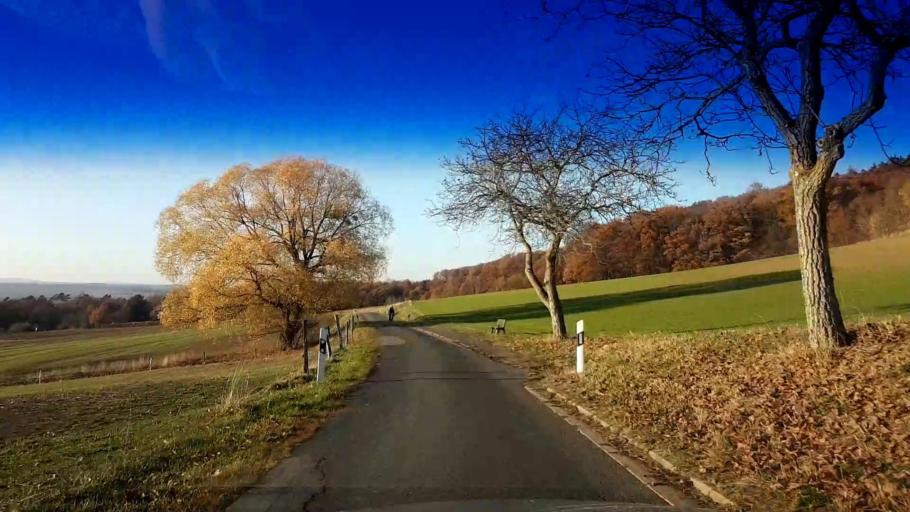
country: DE
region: Bavaria
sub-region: Upper Franconia
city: Schesslitz
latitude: 49.9519
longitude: 11.0419
